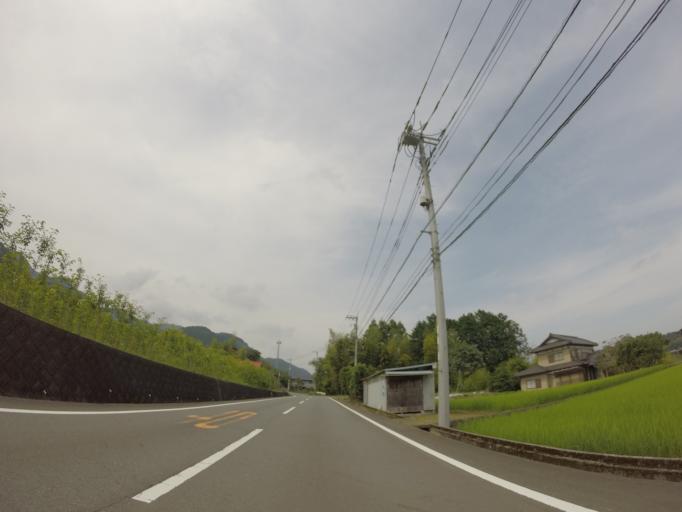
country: JP
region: Shizuoka
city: Fujinomiya
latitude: 35.2658
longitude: 138.5565
